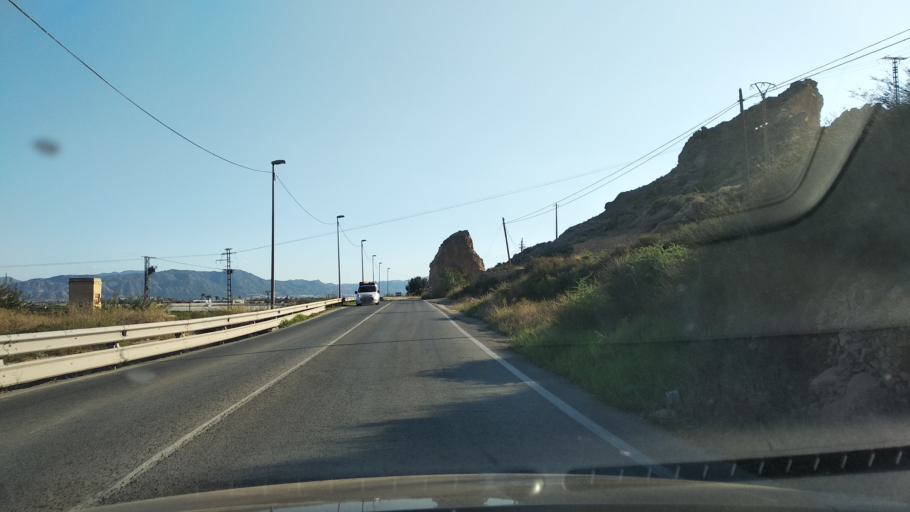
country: ES
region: Murcia
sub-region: Murcia
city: Santomera
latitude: 38.0562
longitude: -1.0524
